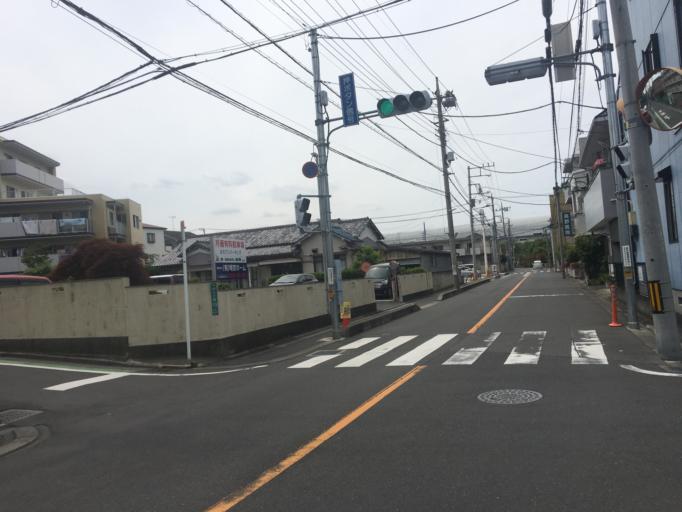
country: JP
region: Saitama
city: Shimotoda
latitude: 35.8337
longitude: 139.6668
